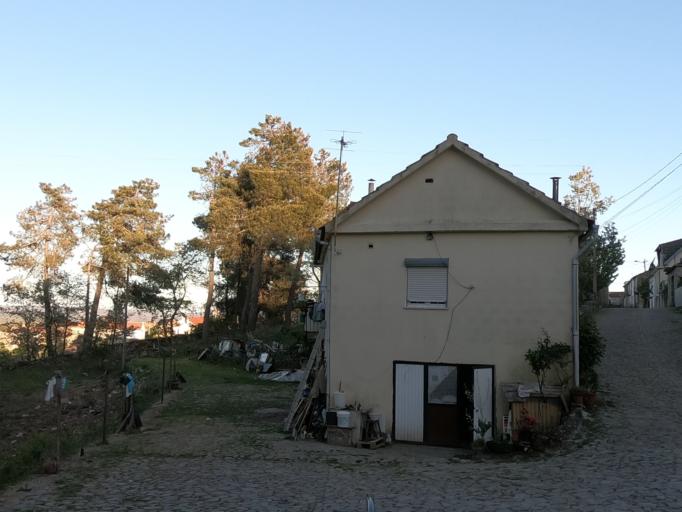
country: PT
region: Vila Real
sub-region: Sabrosa
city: Sabrosa
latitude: 41.3496
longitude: -7.6231
